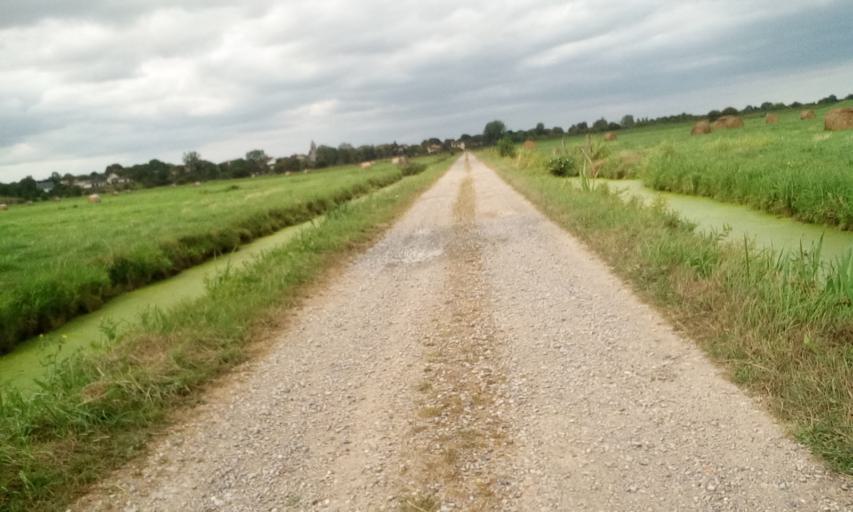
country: FR
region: Lower Normandy
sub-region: Departement du Calvados
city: Troarn
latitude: 49.1927
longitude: -0.1681
